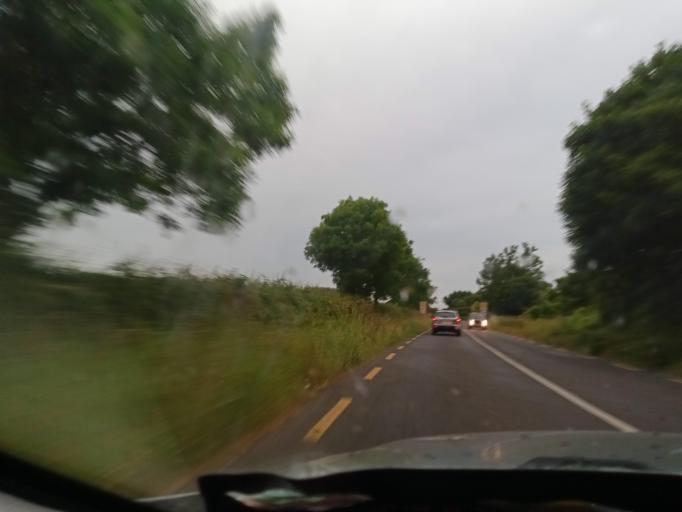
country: IE
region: Leinster
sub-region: Laois
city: Mountmellick
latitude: 53.1225
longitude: -7.3723
